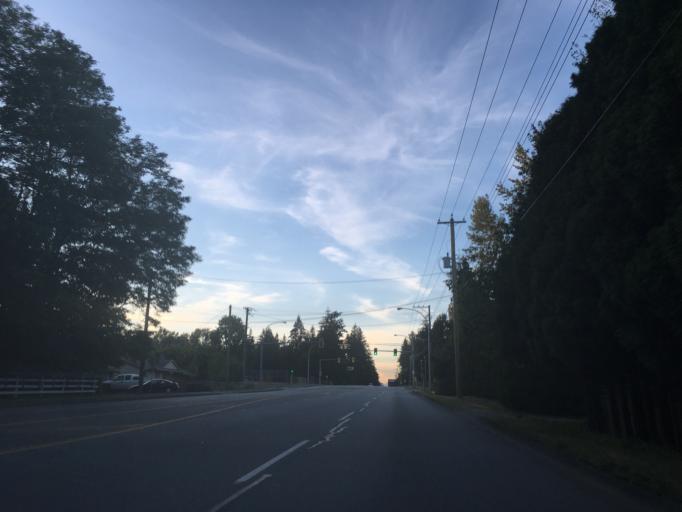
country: US
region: Washington
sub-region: Whatcom County
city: Blaine
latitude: 49.0374
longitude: -122.7351
